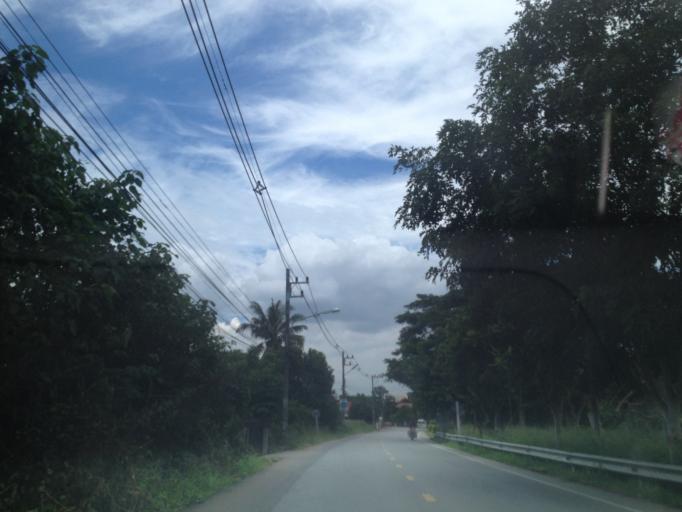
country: TH
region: Chiang Mai
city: Saraphi
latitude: 18.7306
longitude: 98.9844
